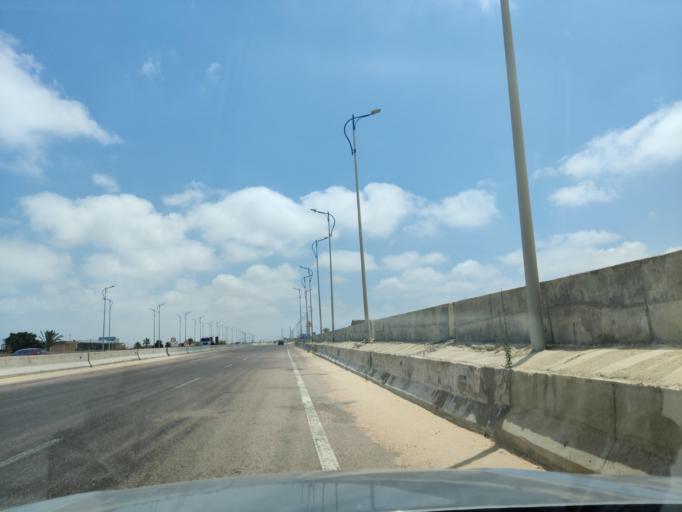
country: EG
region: Alexandria
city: Alexandria
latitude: 30.9599
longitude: 29.5420
